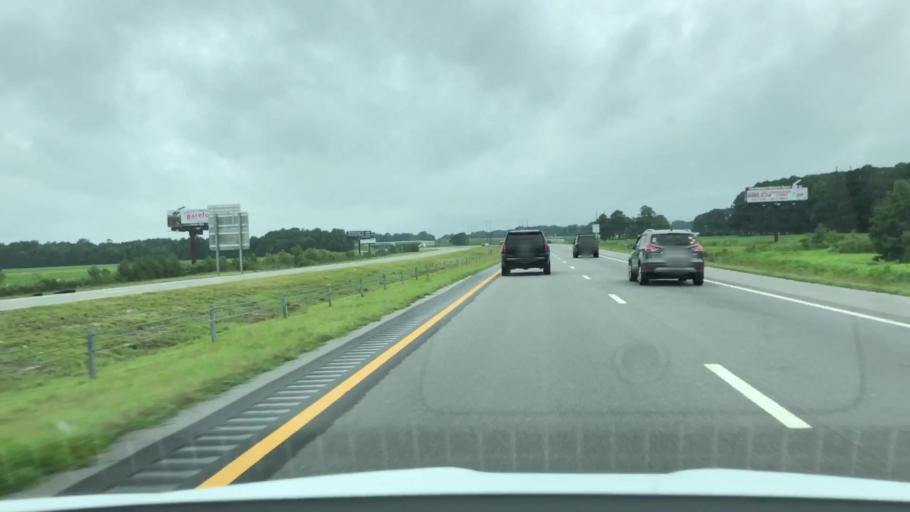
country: US
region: North Carolina
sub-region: Wayne County
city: Elroy
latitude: 35.4168
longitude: -77.9108
